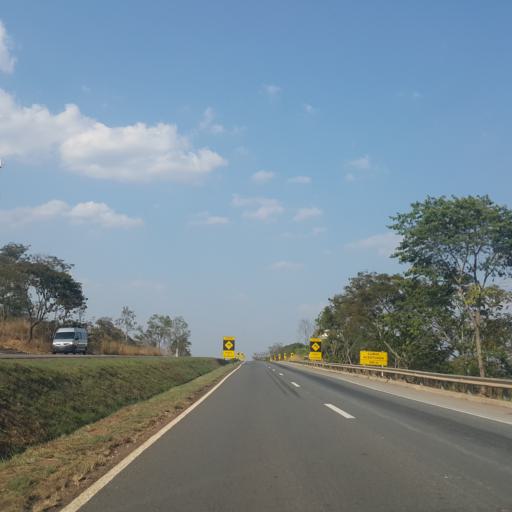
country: BR
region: Goias
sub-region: Abadiania
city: Abadiania
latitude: -16.1618
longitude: -48.6197
